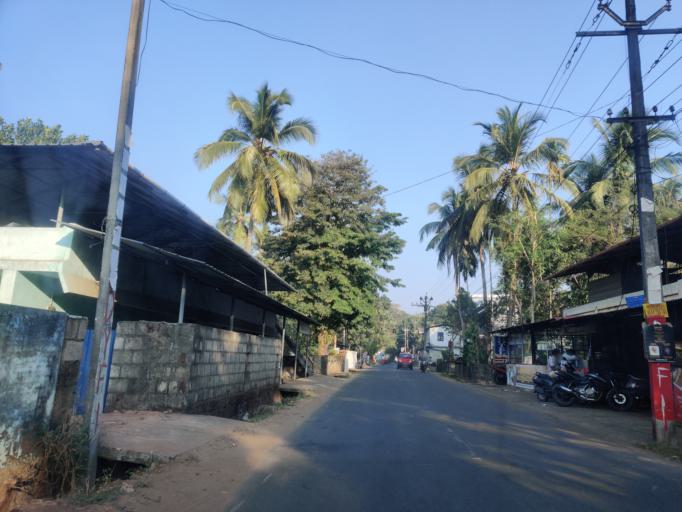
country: IN
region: Kerala
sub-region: Malappuram
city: Ponnani
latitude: 10.7332
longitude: 76.0159
